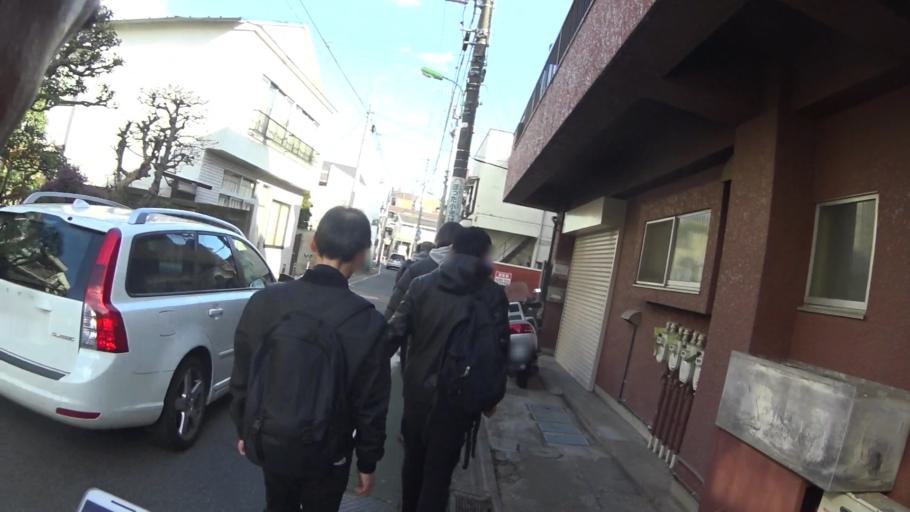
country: JP
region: Tokyo
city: Mitaka-shi
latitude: 35.6552
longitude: 139.6084
